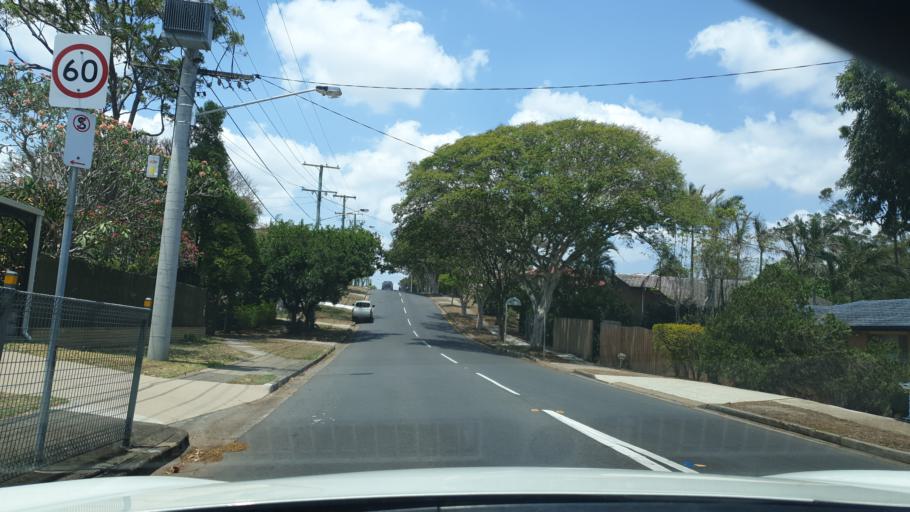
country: AU
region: Queensland
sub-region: Brisbane
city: Zillmere
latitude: -27.3654
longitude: 153.0264
